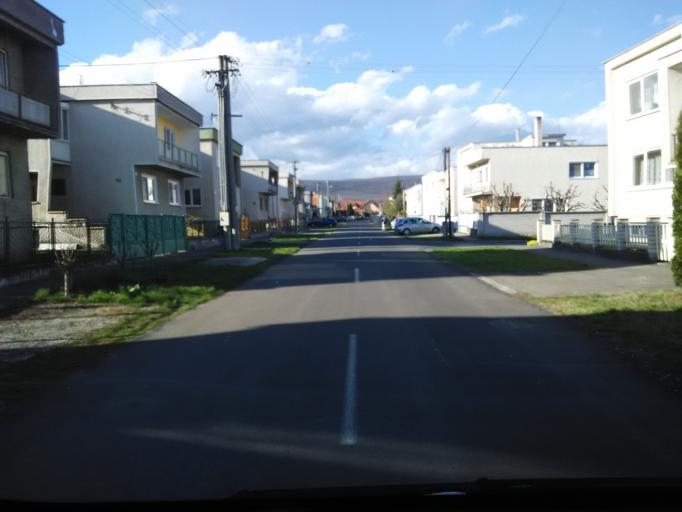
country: SK
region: Nitriansky
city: Tlmace
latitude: 48.2895
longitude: 18.5972
